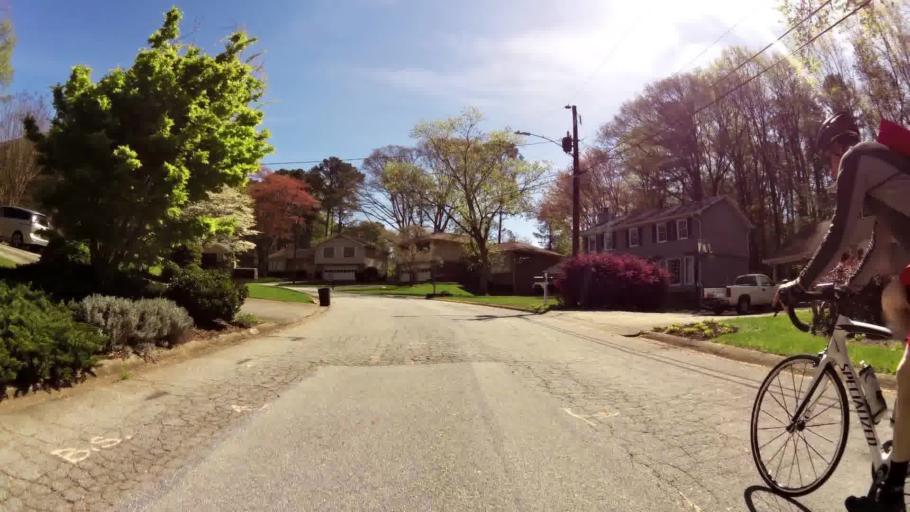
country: US
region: Georgia
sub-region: DeKalb County
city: Clarkston
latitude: 33.8272
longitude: -84.2608
